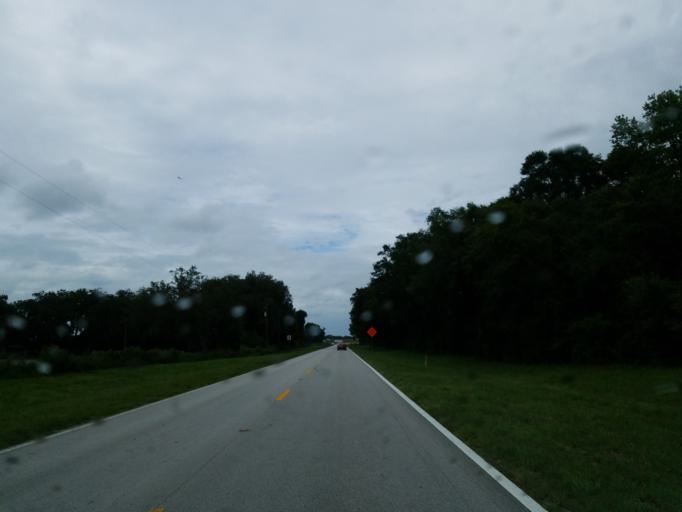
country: US
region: Florida
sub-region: Sumter County
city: Lake Panasoffkee
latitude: 28.7441
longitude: -82.1038
